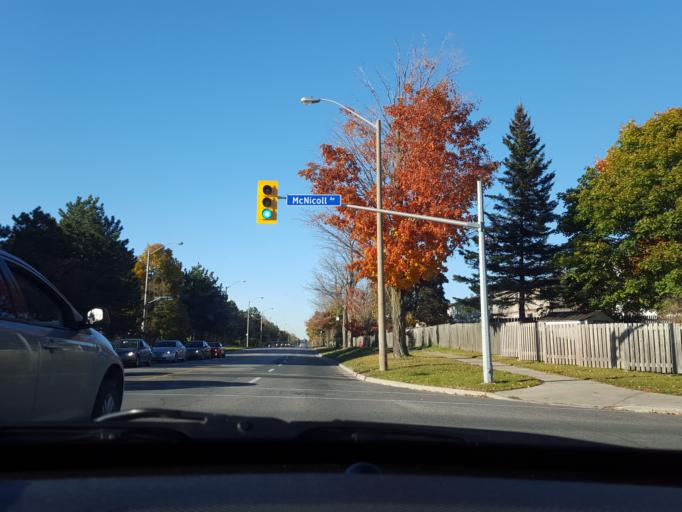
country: CA
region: Ontario
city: Scarborough
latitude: 43.8156
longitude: -79.2817
